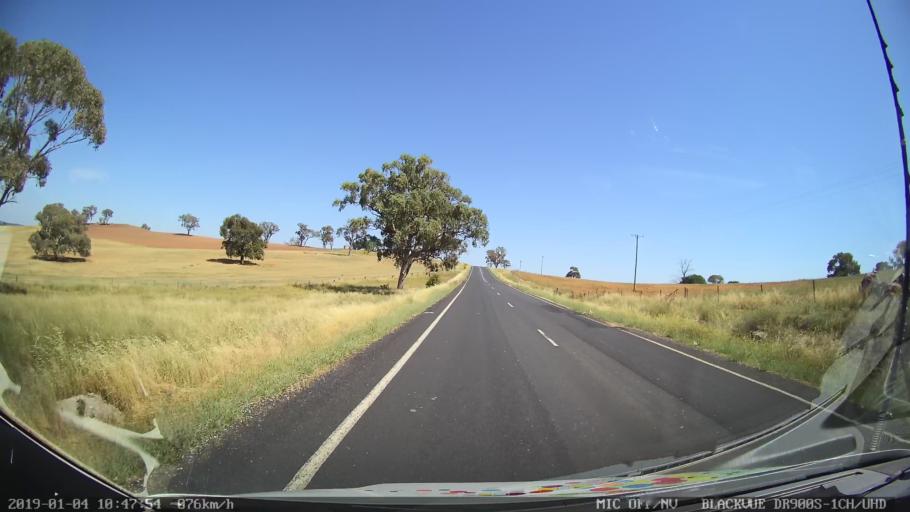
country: AU
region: New South Wales
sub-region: Cabonne
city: Molong
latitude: -33.2653
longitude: 148.7165
